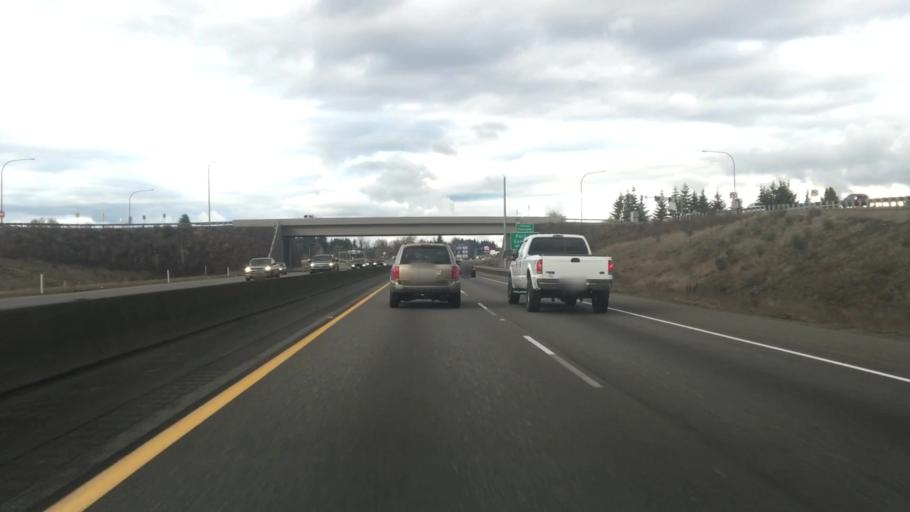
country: US
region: Washington
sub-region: Lewis County
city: Centralia
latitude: 46.7054
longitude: -122.9735
